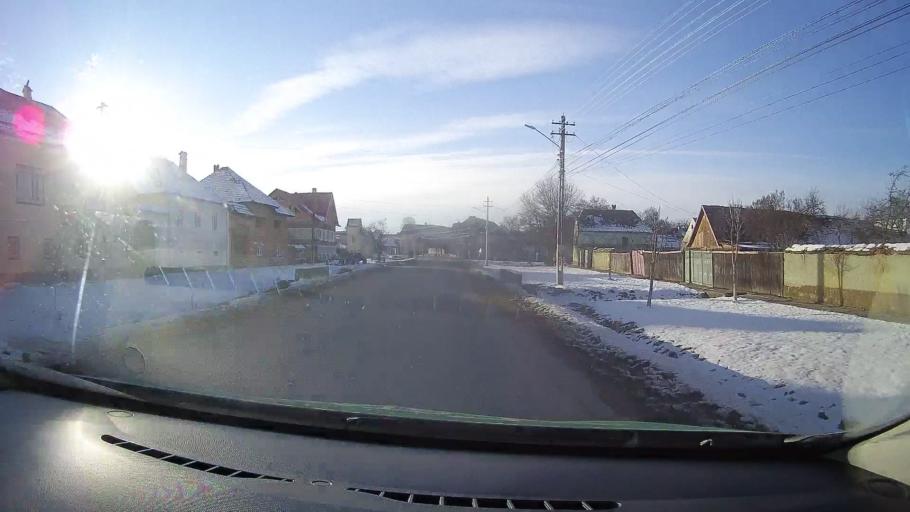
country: RO
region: Sibiu
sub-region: Comuna Merghindeal
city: Merghindeal
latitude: 45.9664
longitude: 24.7219
